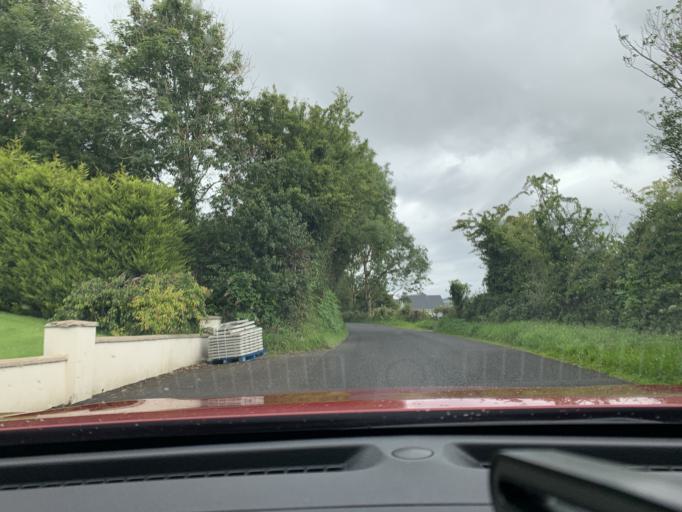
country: IE
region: Connaught
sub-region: County Leitrim
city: Manorhamilton
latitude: 54.3094
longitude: -8.1884
